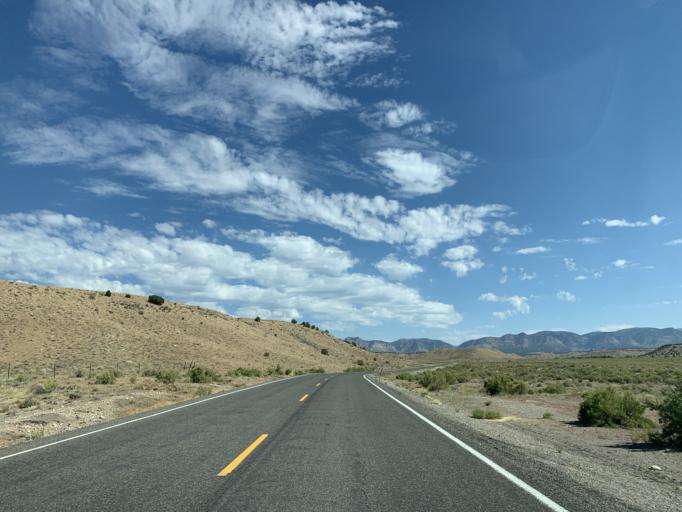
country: US
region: Utah
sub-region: Carbon County
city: Wellington
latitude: 39.5726
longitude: -110.6536
